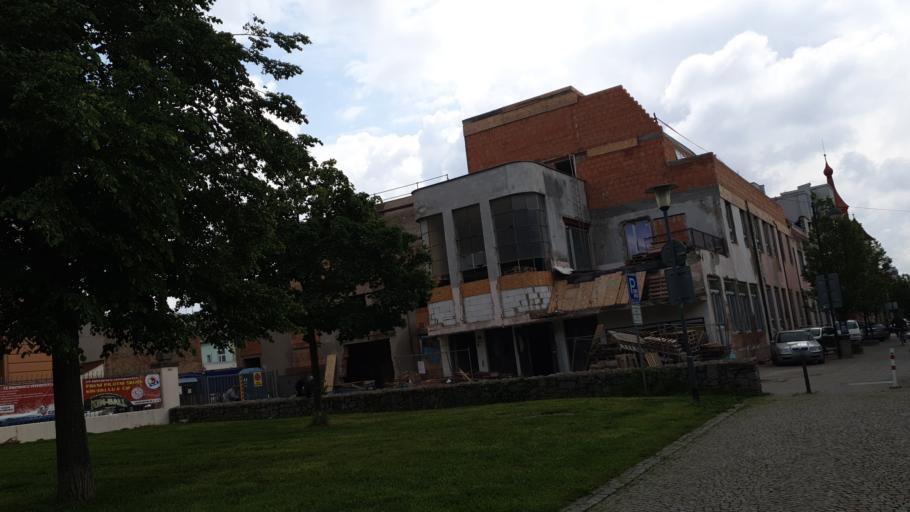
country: CZ
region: Pardubicky
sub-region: Okres Pardubice
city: Pardubice
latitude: 50.0351
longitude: 15.7716
